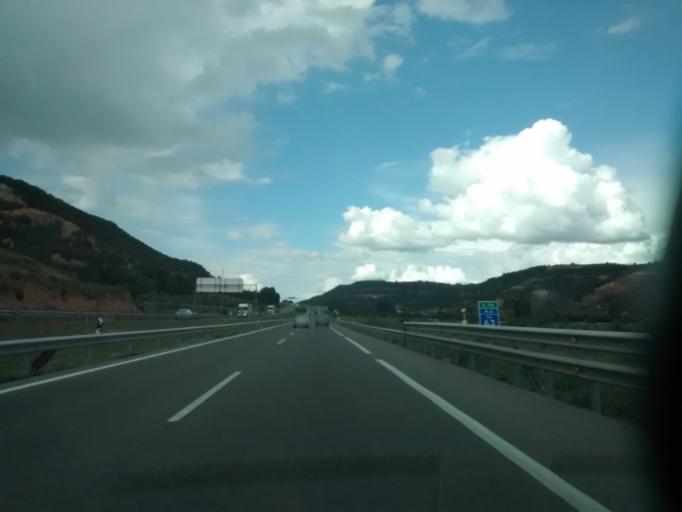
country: ES
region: Castille-La Mancha
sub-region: Provincia de Guadalajara
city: Tortola de Henares
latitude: 40.6737
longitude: -3.1012
